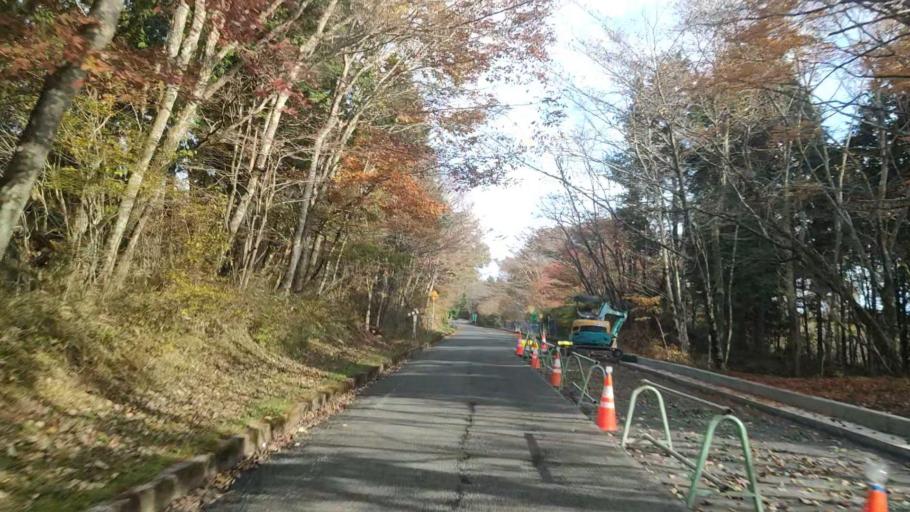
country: JP
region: Shizuoka
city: Fujinomiya
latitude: 35.2982
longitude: 138.6967
